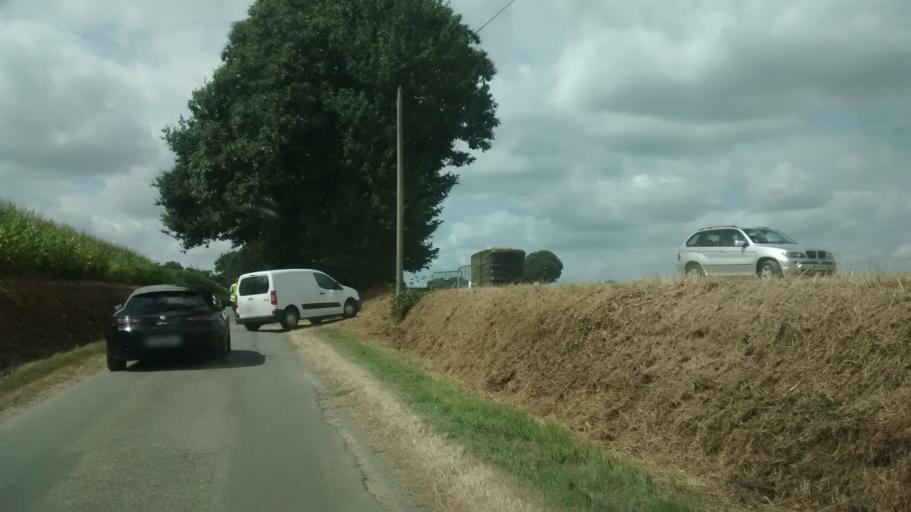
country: FR
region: Brittany
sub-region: Departement d'Ille-et-Vilaine
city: Tinteniac
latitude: 48.3091
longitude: -1.8551
